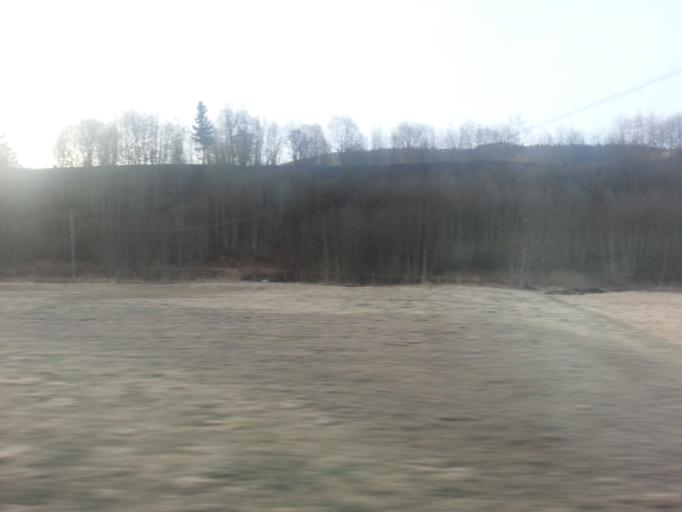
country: NO
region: Sor-Trondelag
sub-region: Melhus
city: Lundamo
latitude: 63.1729
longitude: 10.3046
